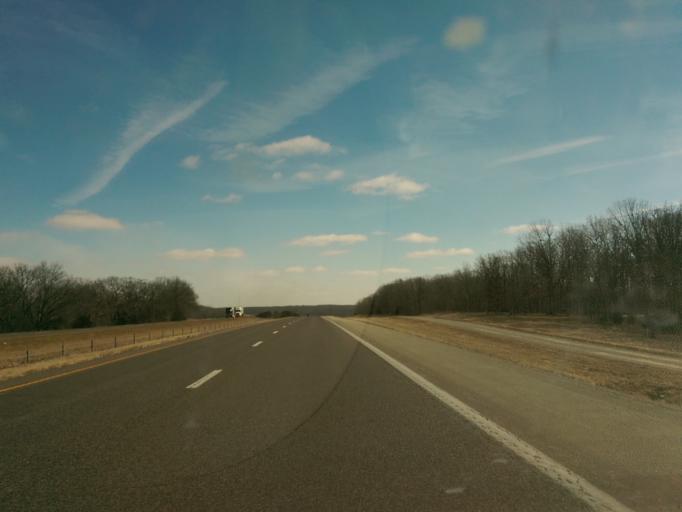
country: US
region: Missouri
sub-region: Callaway County
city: Fulton
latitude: 38.9381
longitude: -91.8607
